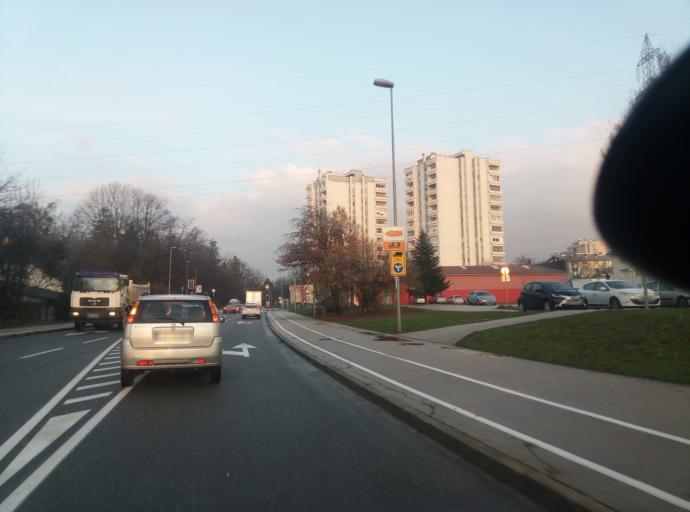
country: SI
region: Kranj
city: Kranj
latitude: 46.2317
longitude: 14.3649
